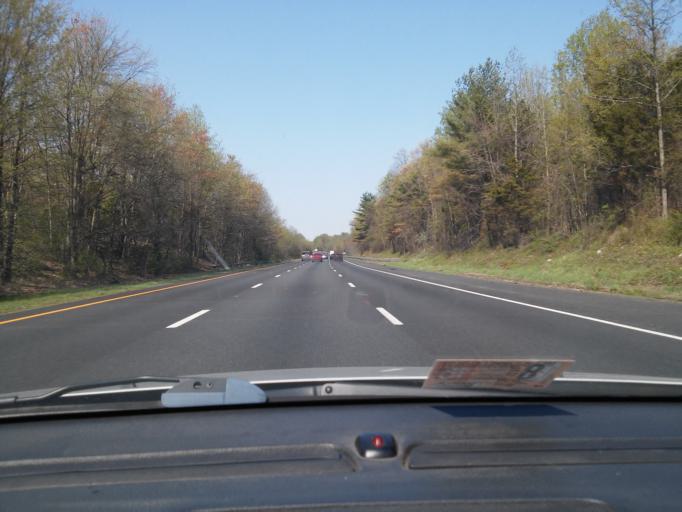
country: US
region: New Jersey
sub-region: Somerset County
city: Watchung
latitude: 40.6495
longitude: -74.4784
